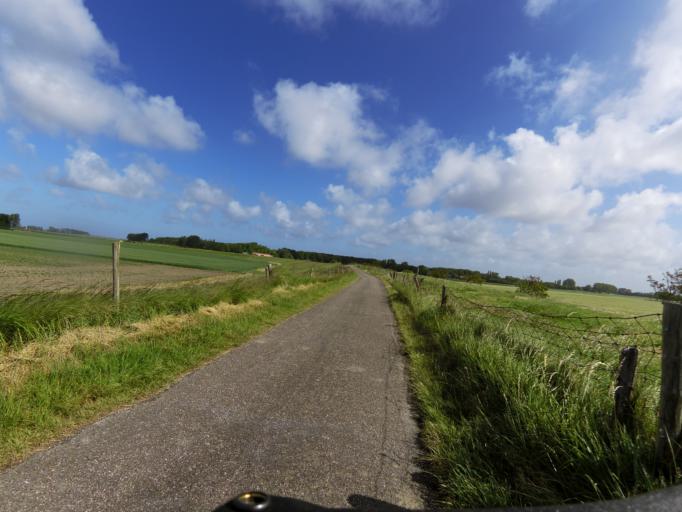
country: NL
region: Zeeland
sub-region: Schouwen-Duiveland
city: Scharendijke
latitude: 51.6679
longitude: 3.9435
